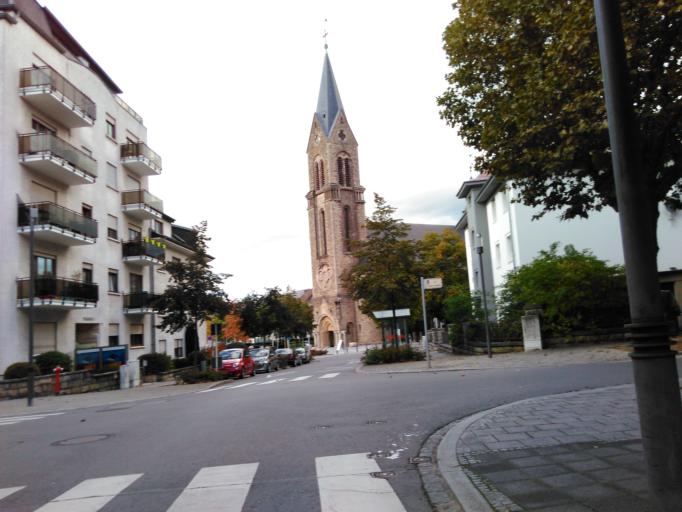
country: LU
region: Luxembourg
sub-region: Canton d'Esch-sur-Alzette
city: Esch-sur-Alzette
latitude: 49.4998
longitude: 5.9752
